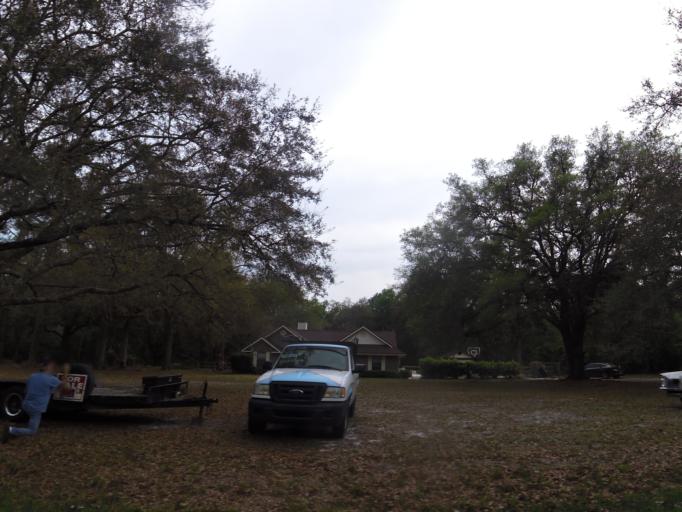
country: US
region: Florida
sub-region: Nassau County
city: Hilliard
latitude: 30.6979
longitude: -81.8999
